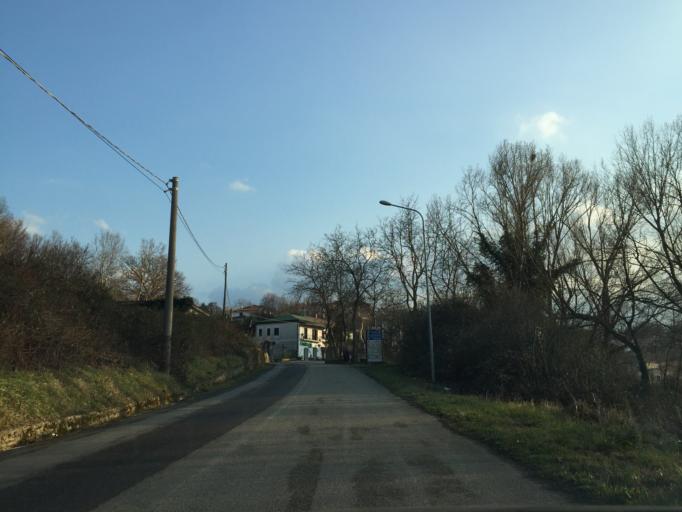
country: IT
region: Campania
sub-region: Provincia di Benevento
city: Arpaise
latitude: 41.0318
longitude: 14.7454
